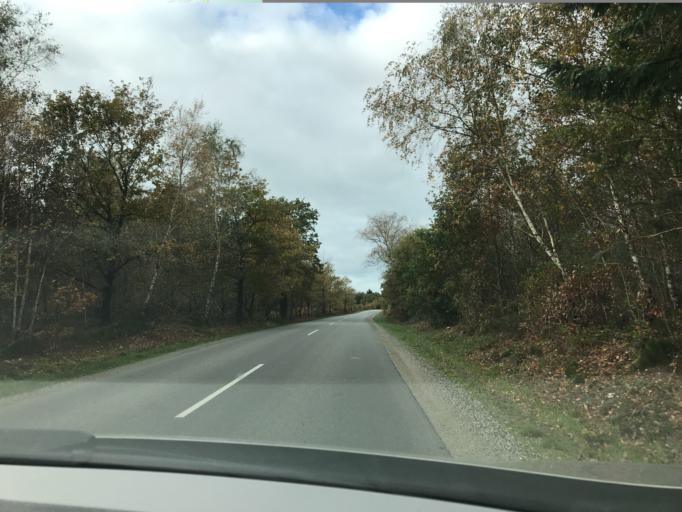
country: DK
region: South Denmark
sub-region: Varde Kommune
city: Olgod
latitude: 55.7945
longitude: 8.7382
